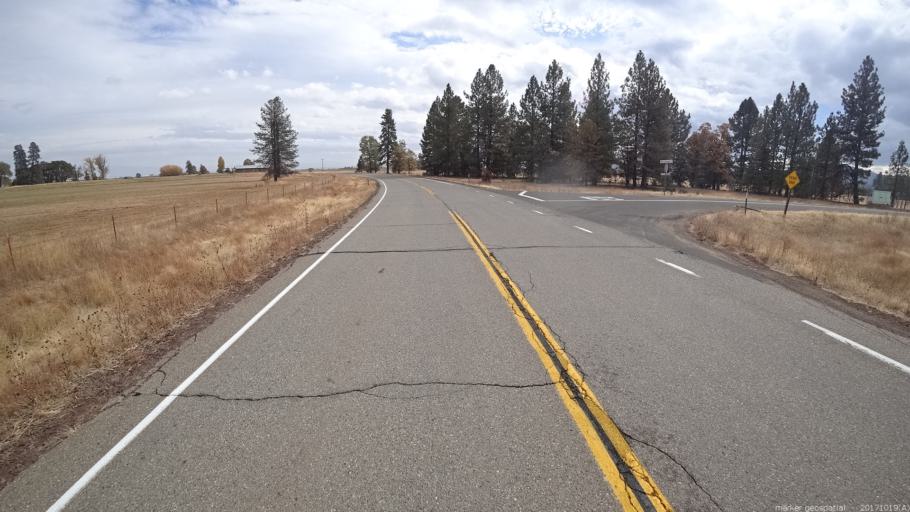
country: US
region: California
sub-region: Shasta County
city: Burney
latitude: 41.0806
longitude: -121.5132
